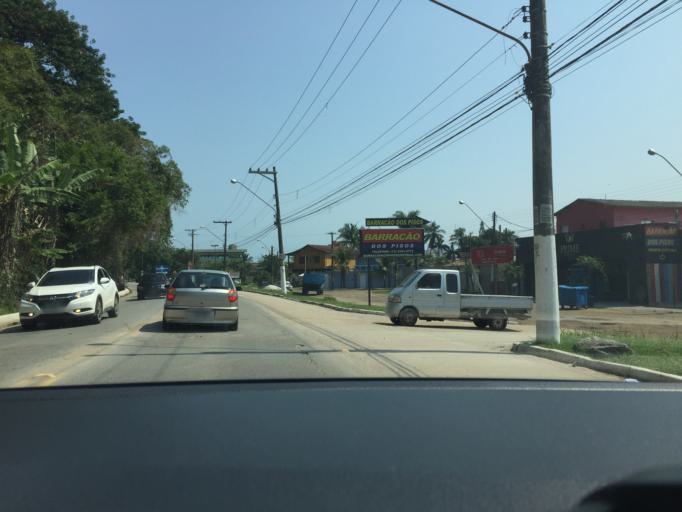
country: BR
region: Sao Paulo
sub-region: Guaruja
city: Guaruja
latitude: -23.9813
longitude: -46.1966
